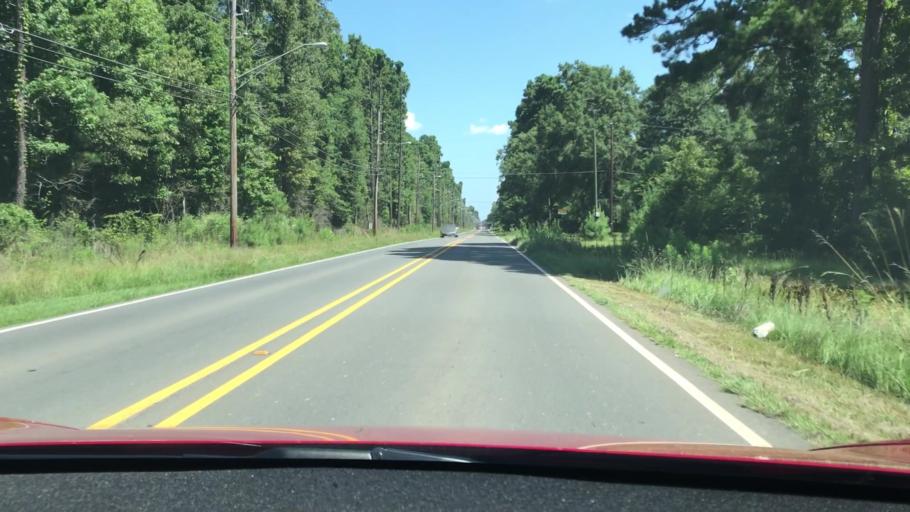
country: US
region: Louisiana
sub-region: De Soto Parish
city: Stonewall
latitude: 32.3474
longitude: -93.7138
